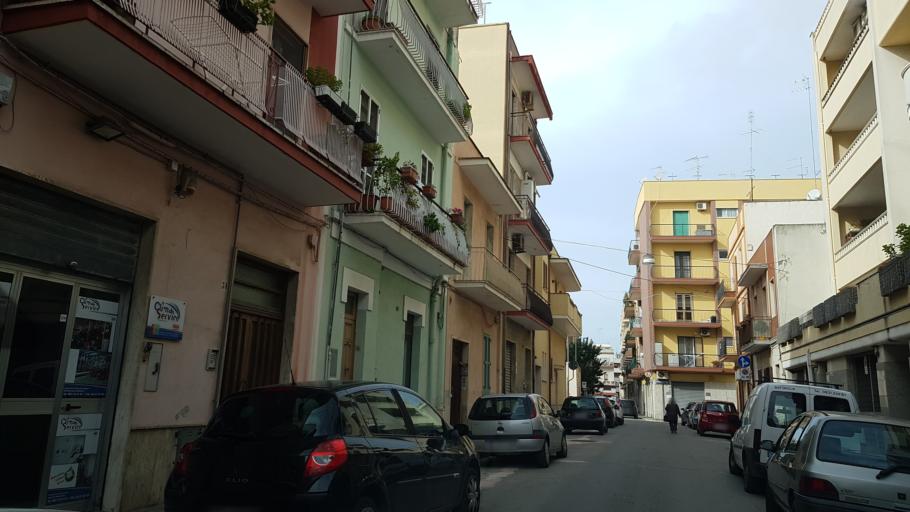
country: IT
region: Apulia
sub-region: Provincia di Brindisi
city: Brindisi
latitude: 40.6321
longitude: 17.9343
